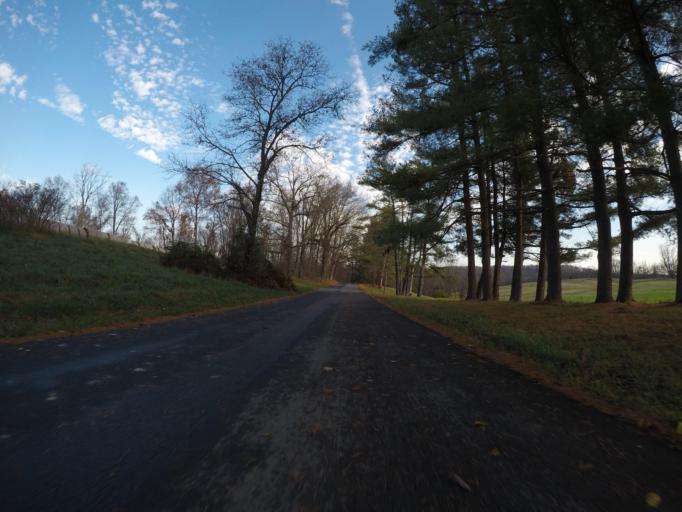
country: US
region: Maryland
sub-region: Carroll County
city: Hampstead
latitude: 39.5526
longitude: -76.8134
